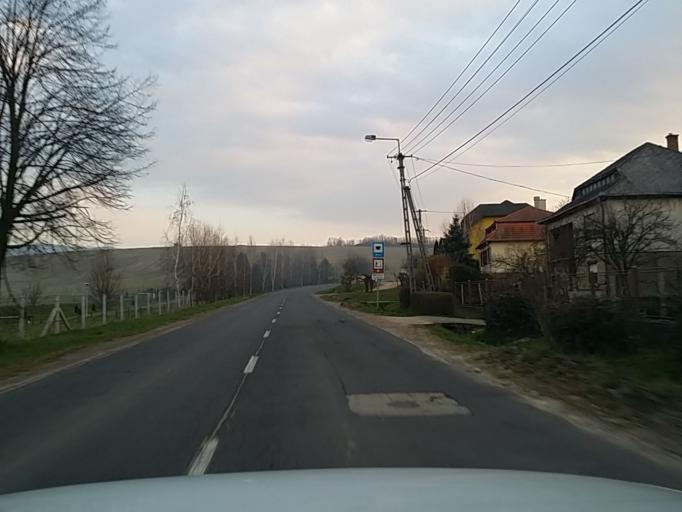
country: HU
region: Nograd
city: Batonyterenye
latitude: 47.9959
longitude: 19.8470
